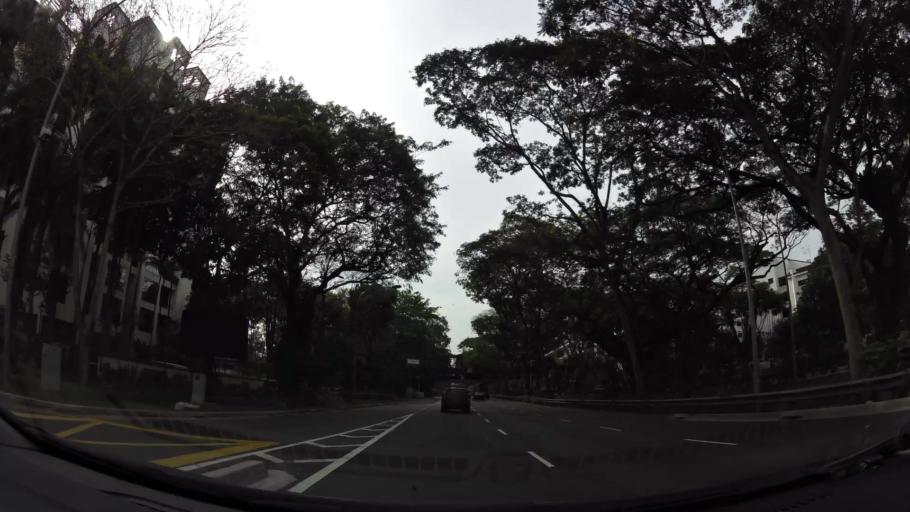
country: SG
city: Singapore
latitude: 1.3363
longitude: 103.7821
